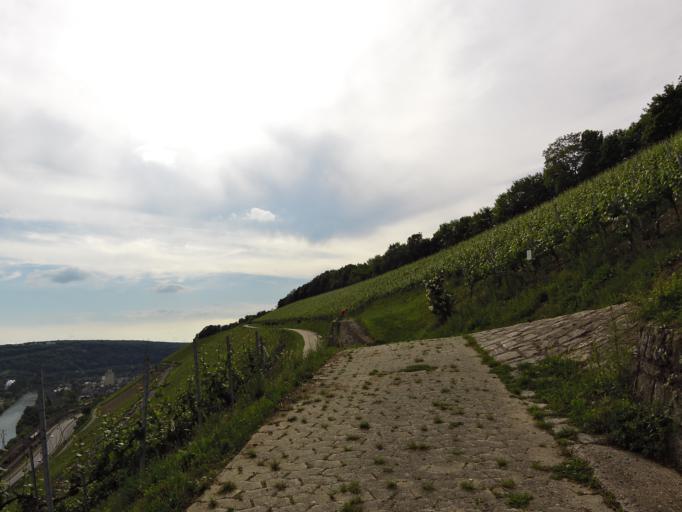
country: DE
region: Bavaria
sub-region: Regierungsbezirk Unterfranken
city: Hochberg
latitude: 49.8056
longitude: 9.9112
